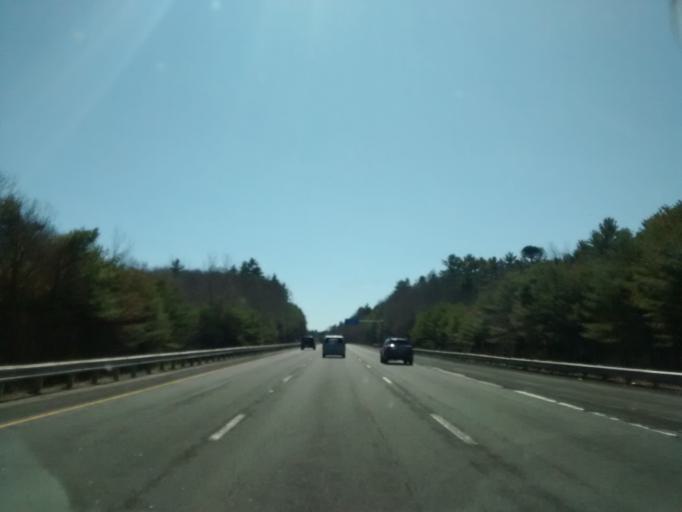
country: US
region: Massachusetts
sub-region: Worcester County
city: Sturbridge
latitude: 42.0895
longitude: -72.0925
